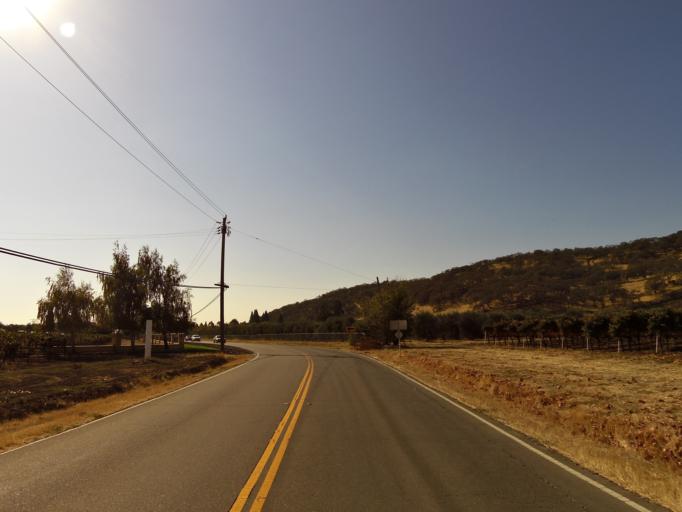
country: US
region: California
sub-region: Solano County
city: Green Valley
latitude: 38.2545
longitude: -122.1197
